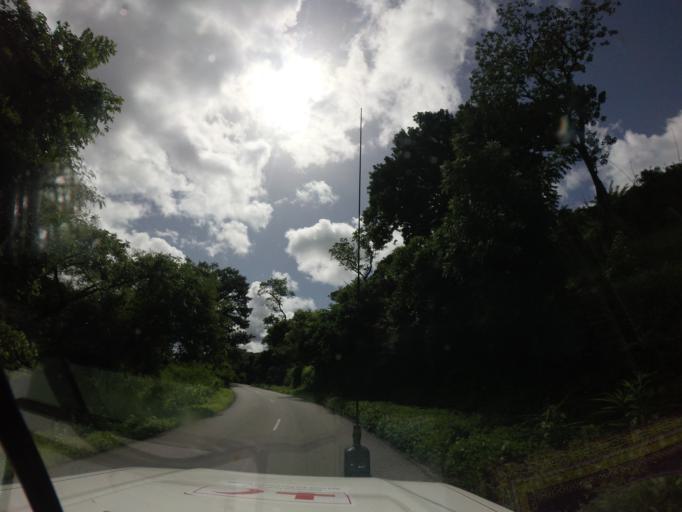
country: GN
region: Mamou
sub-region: Mamou Prefecture
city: Mamou
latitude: 10.2895
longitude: -11.9347
